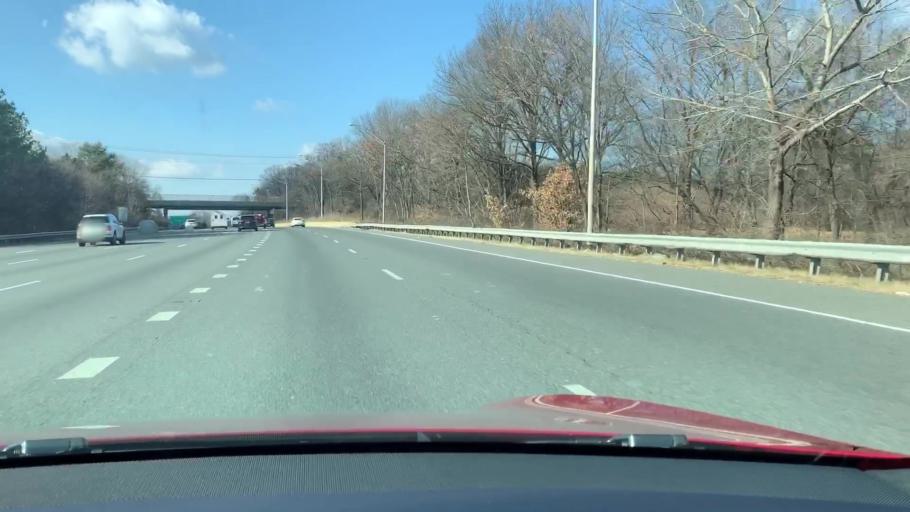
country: US
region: Maryland
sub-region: Prince George's County
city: Beltsville
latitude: 39.0223
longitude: -76.9369
